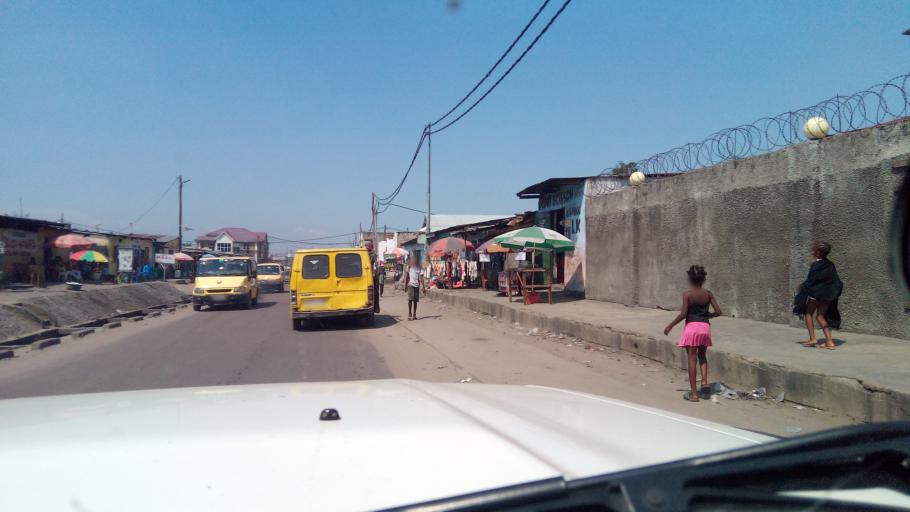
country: CD
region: Kinshasa
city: Kinshasa
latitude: -4.3663
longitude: 15.2986
